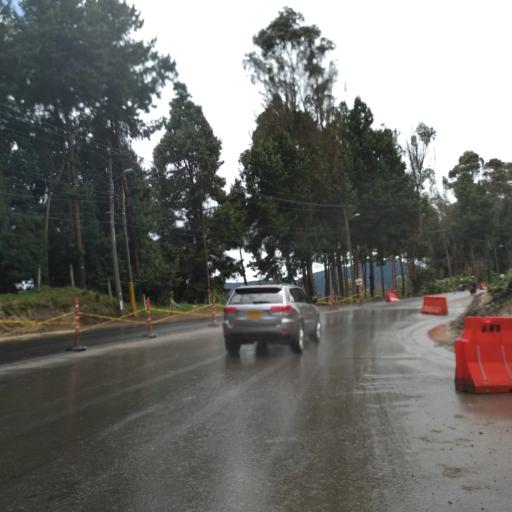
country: CO
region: Bogota D.C.
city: Barrio San Luis
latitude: 4.6843
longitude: -73.9898
